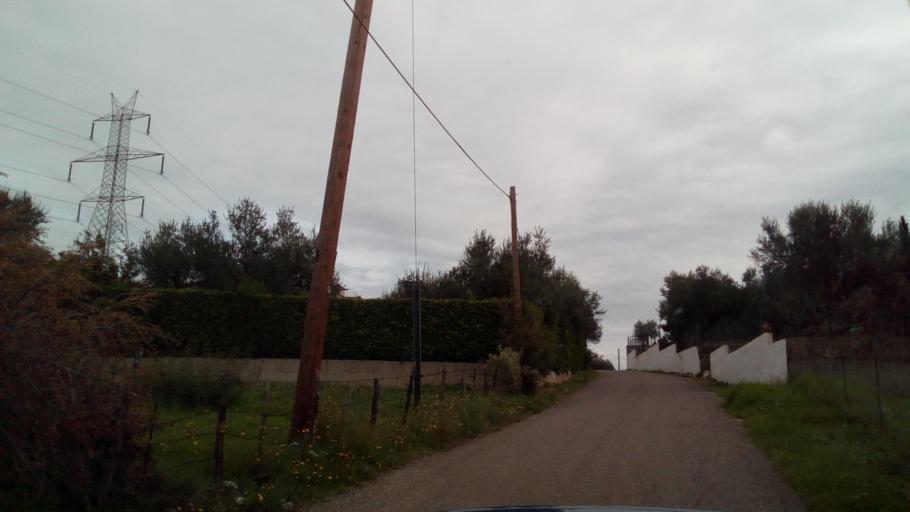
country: GR
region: West Greece
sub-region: Nomos Achaias
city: Kamarai
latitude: 38.4100
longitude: 21.9500
